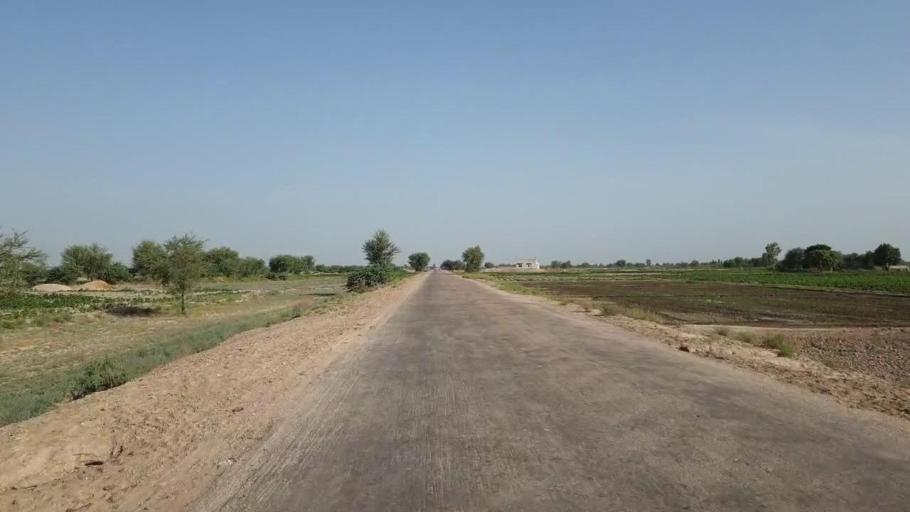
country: PK
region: Sindh
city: Nawabshah
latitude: 26.1440
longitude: 68.4506
